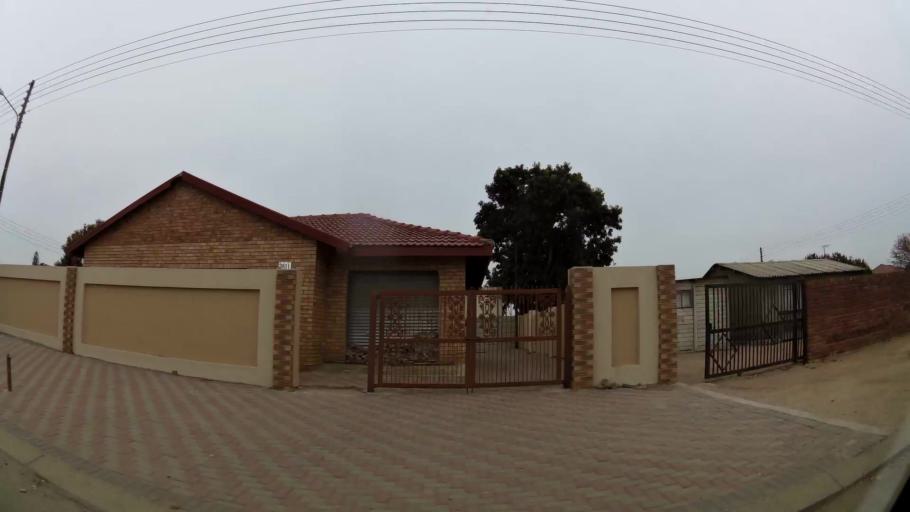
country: ZA
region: Limpopo
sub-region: Capricorn District Municipality
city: Polokwane
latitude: -23.8495
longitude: 29.3958
